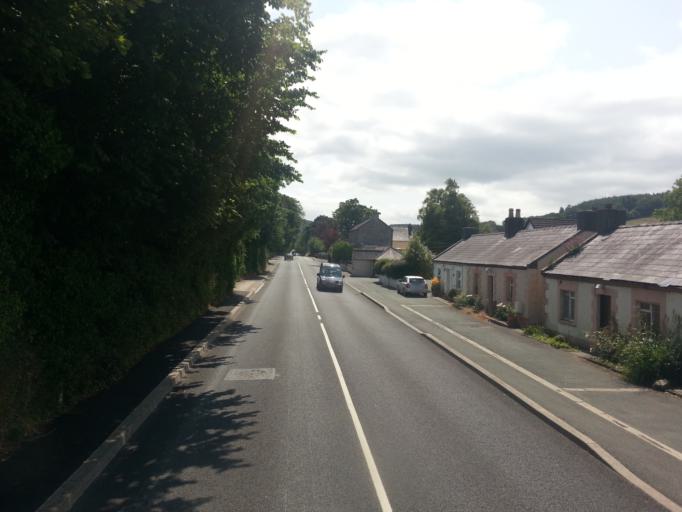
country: IE
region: Leinster
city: Foxrock
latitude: 53.2334
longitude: -6.1898
